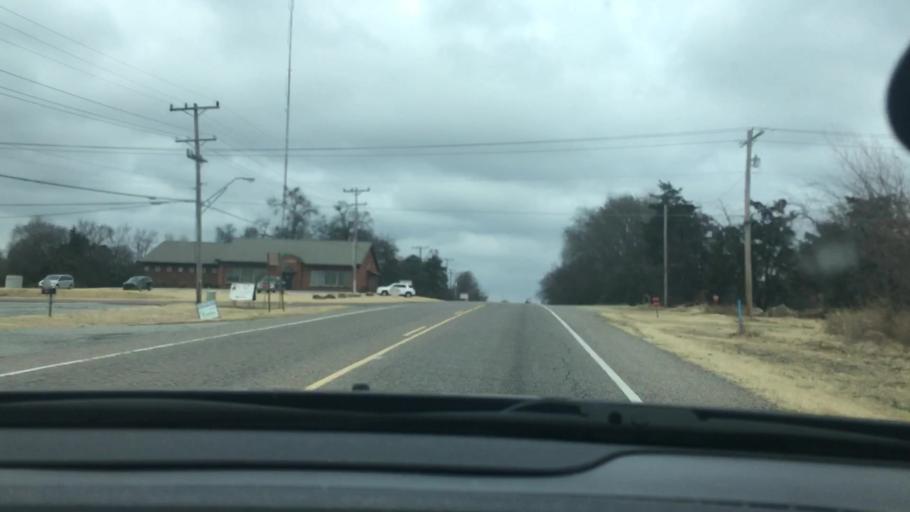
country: US
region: Oklahoma
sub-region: Bryan County
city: Durant
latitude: 34.0260
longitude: -96.3728
